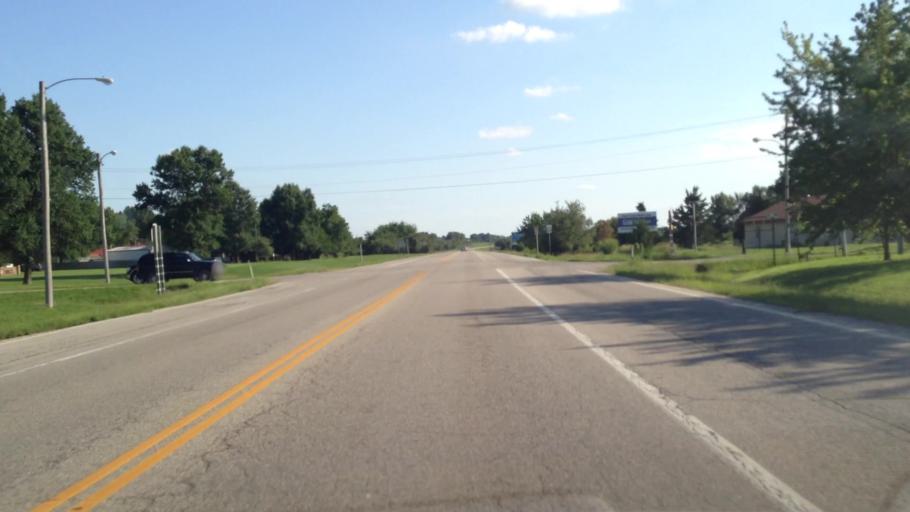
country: US
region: Kansas
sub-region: Crawford County
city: Arma
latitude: 37.5434
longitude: -94.7102
